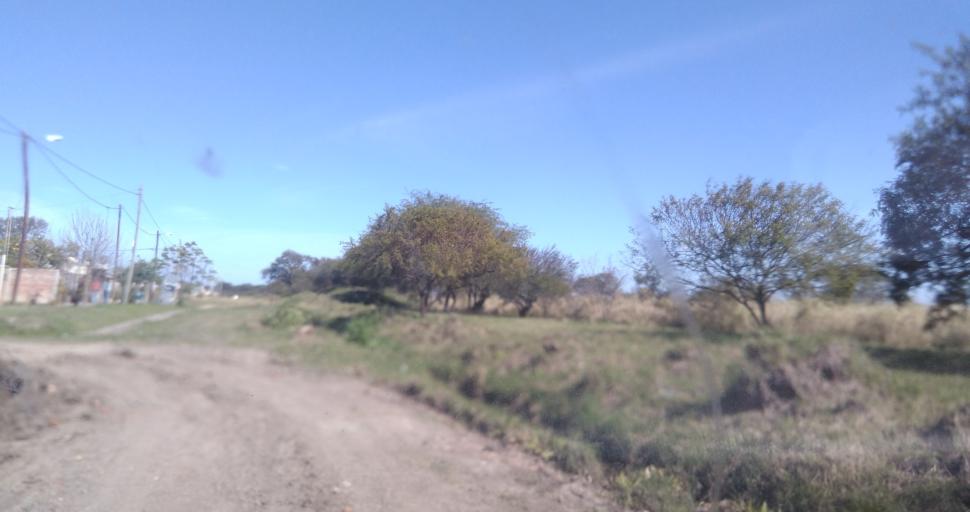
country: AR
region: Chaco
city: Fontana
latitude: -27.4543
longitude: -59.0492
